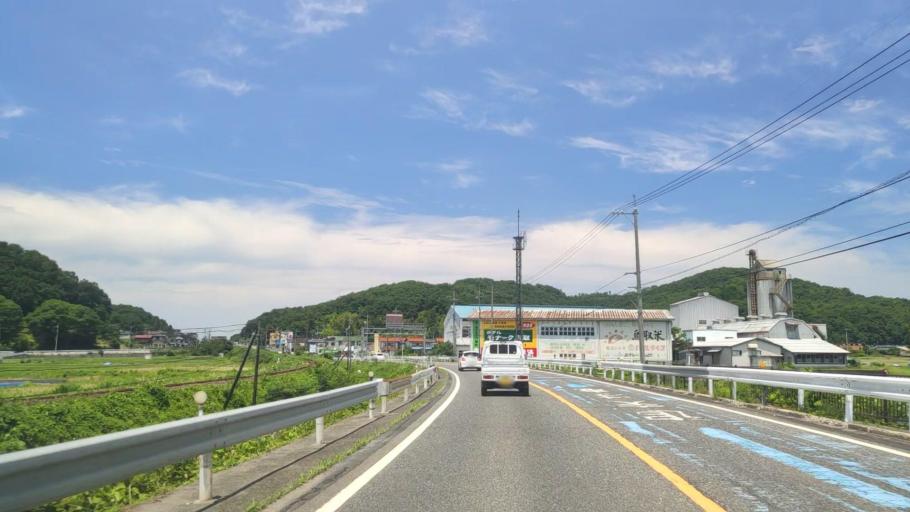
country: JP
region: Tottori
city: Tottori
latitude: 35.4233
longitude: 134.2623
